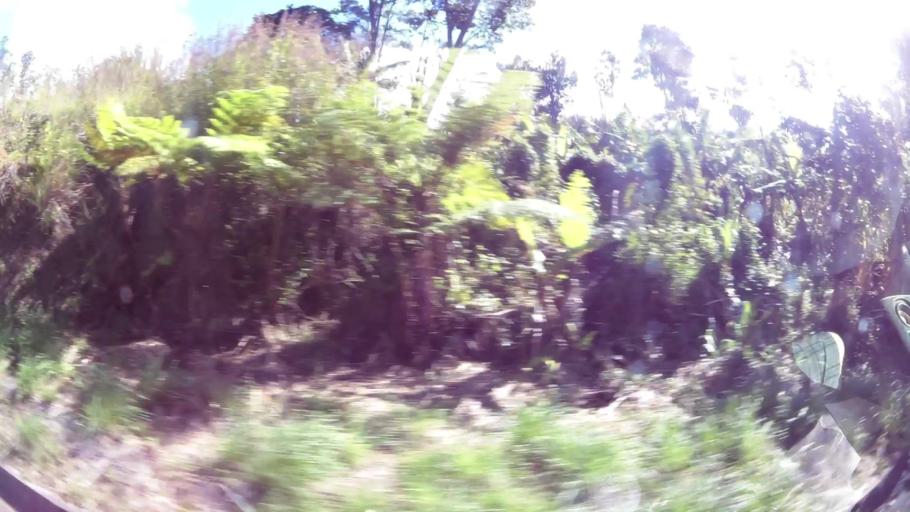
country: DM
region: Saint Paul
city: Pont Casse
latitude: 15.3664
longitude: -61.3548
